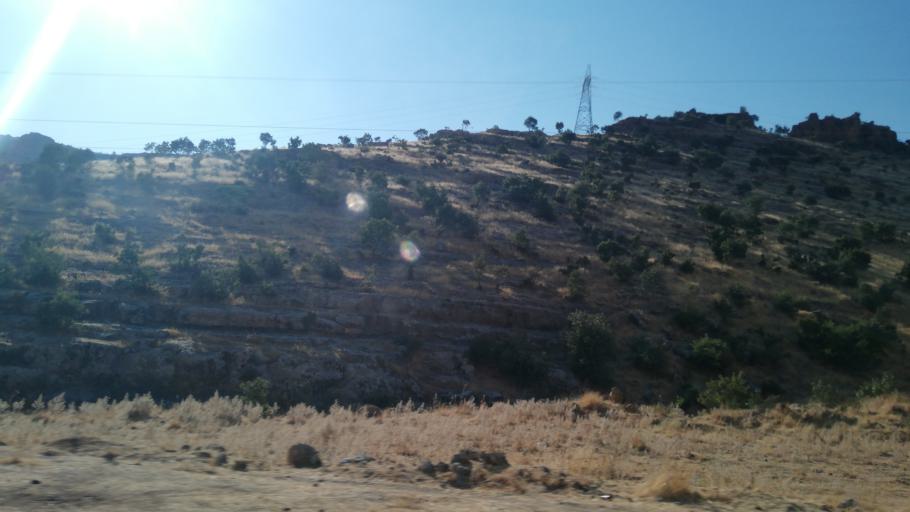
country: TR
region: Mardin
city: Sivrice
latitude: 37.2484
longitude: 41.3558
